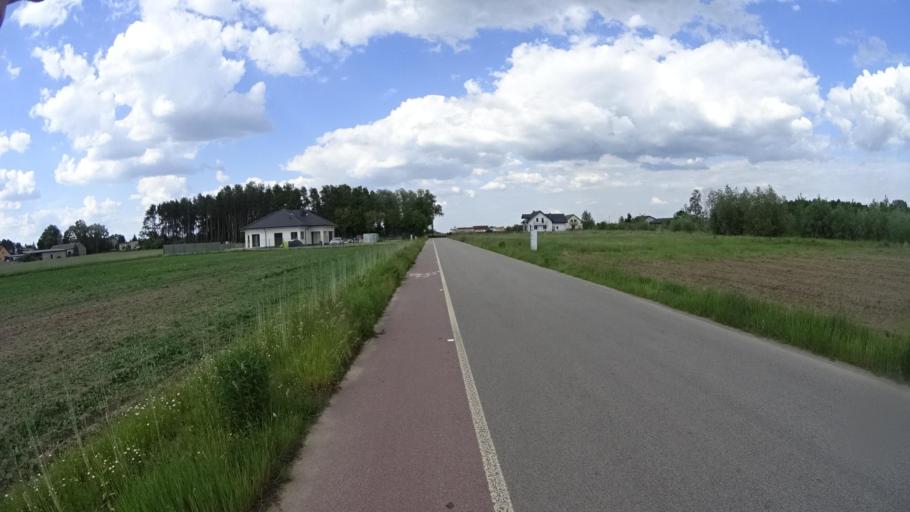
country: PL
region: Masovian Voivodeship
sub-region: Powiat piaseczynski
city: Tarczyn
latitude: 52.0058
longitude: 20.8309
